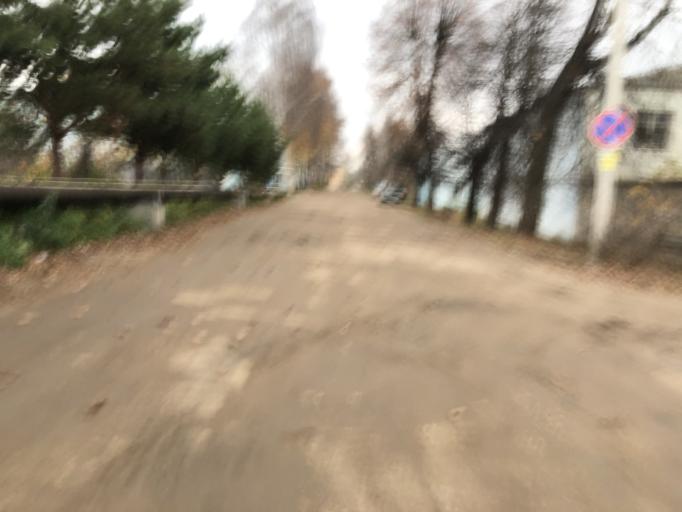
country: RU
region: Tverskaya
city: Rzhev
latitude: 56.2554
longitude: 34.3245
